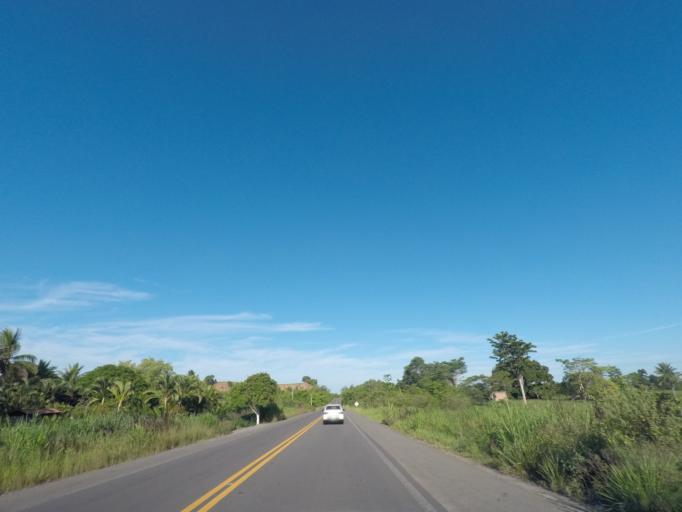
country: BR
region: Bahia
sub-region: Nazare
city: Nazare
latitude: -13.0167
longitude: -38.9830
